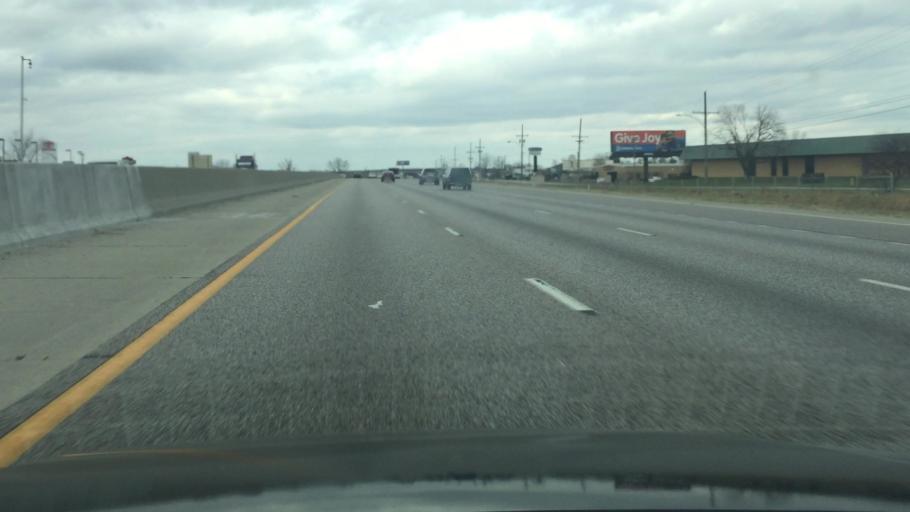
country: US
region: Kansas
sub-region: Johnson County
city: Olathe
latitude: 38.8891
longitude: -94.7896
